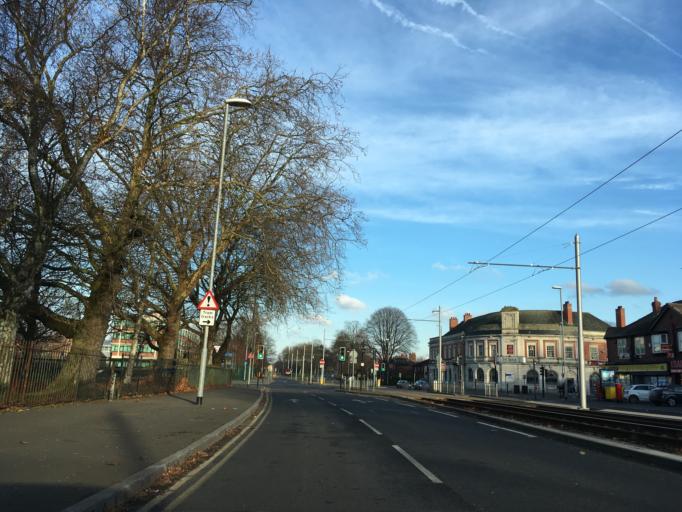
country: GB
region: England
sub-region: Manchester
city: Chorlton cum Hardy
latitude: 53.4341
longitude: -2.2660
